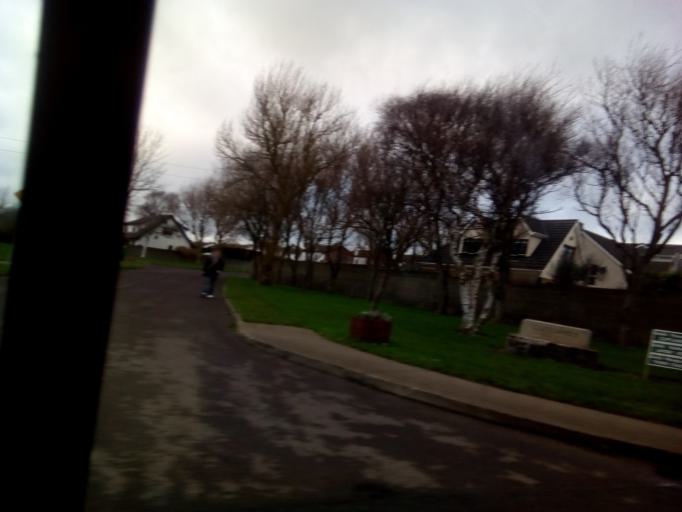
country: IE
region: Leinster
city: An Ros
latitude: 53.5337
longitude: -6.0907
